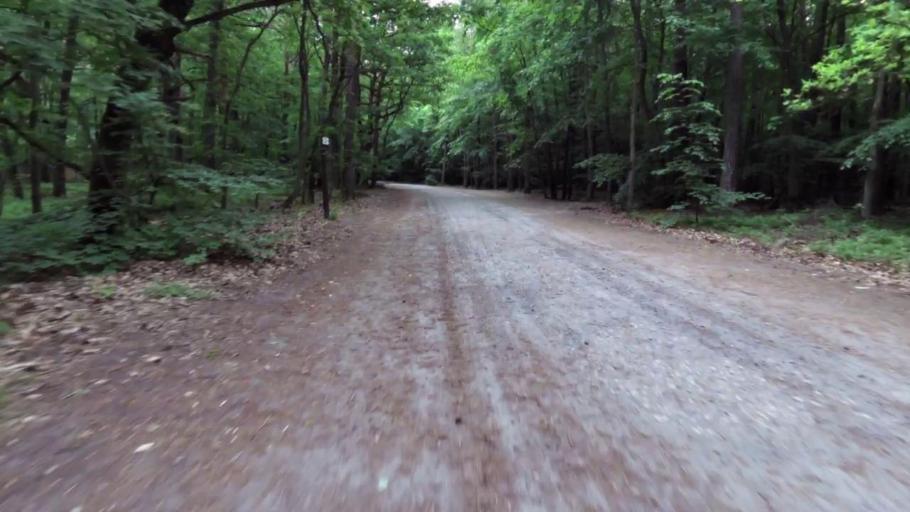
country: PL
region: West Pomeranian Voivodeship
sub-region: Powiat kamienski
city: Miedzyzdroje
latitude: 53.9326
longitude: 14.4719
